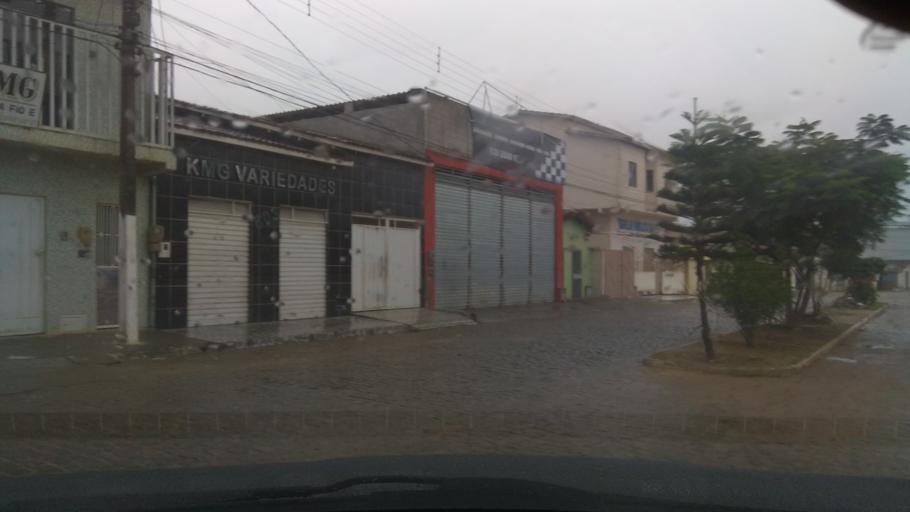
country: BR
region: Bahia
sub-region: Jaguaquara
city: Jaguaquara
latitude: -13.5119
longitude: -40.0598
